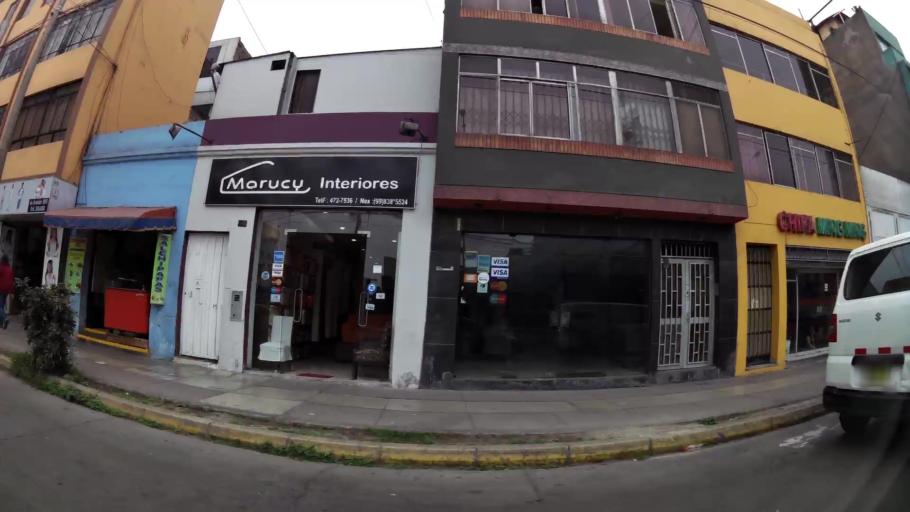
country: PE
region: Lima
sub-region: Lima
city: San Isidro
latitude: -12.0834
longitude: -77.0358
